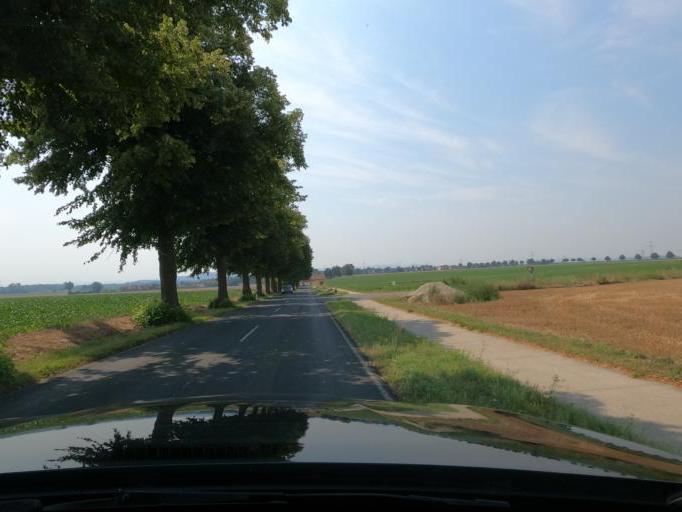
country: DE
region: Lower Saxony
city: Sarstedt
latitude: 52.2247
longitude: 9.8064
